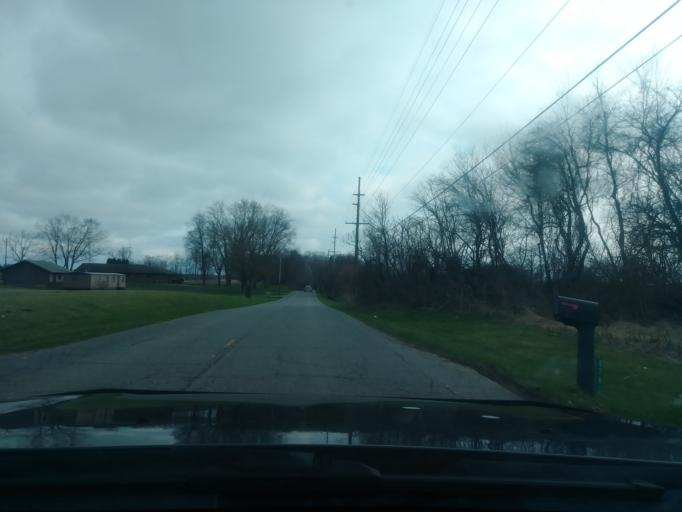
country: US
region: Indiana
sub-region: LaPorte County
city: LaPorte
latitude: 41.6182
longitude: -86.7964
